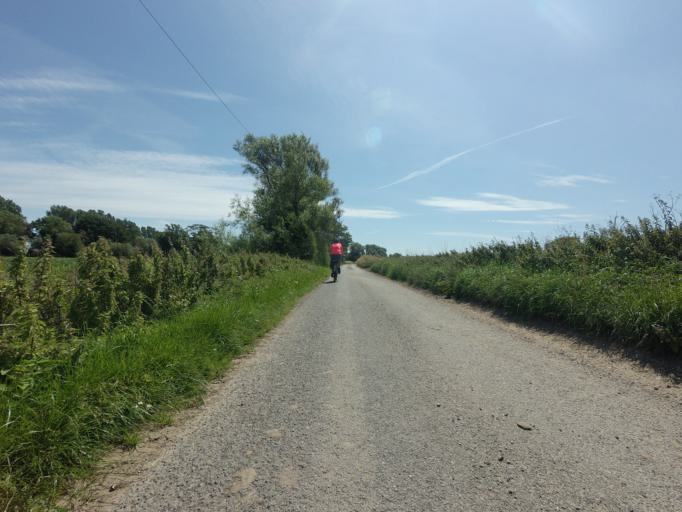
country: GB
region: England
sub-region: Kent
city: Lydd
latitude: 50.9821
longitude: 0.8793
